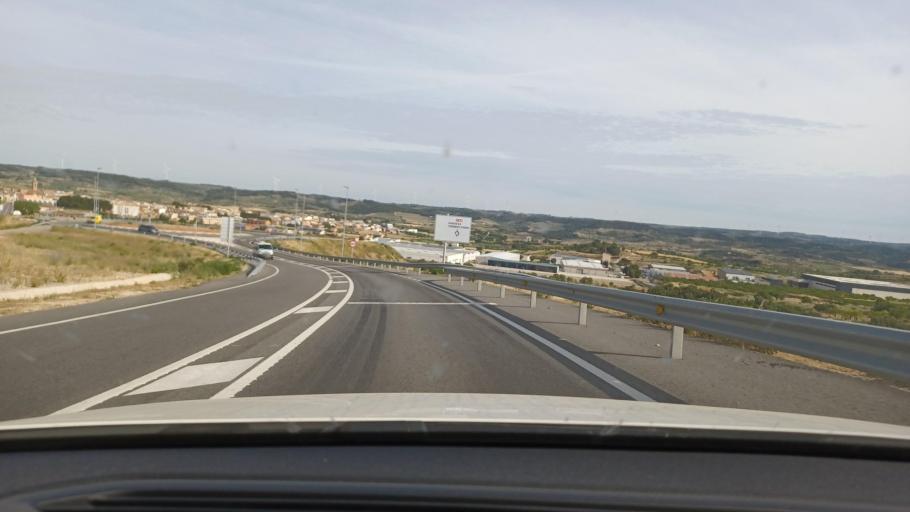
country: ES
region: Catalonia
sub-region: Provincia de Tarragona
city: Gandesa
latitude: 41.0462
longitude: 0.4522
